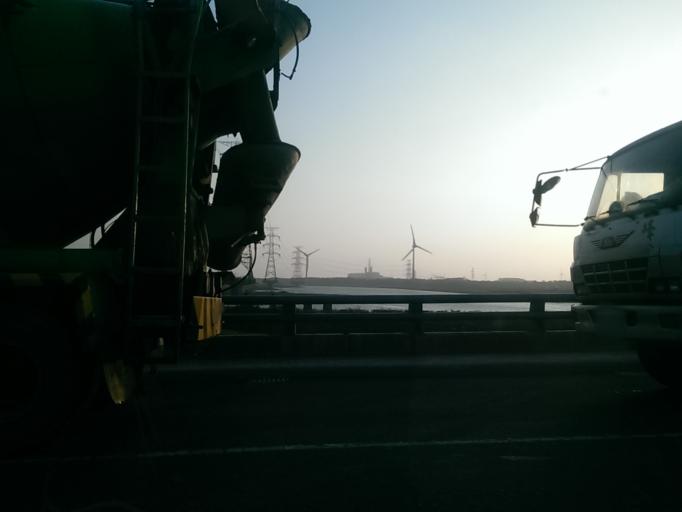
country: TW
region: Taiwan
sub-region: Changhua
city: Chang-hua
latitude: 24.1413
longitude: 120.4451
